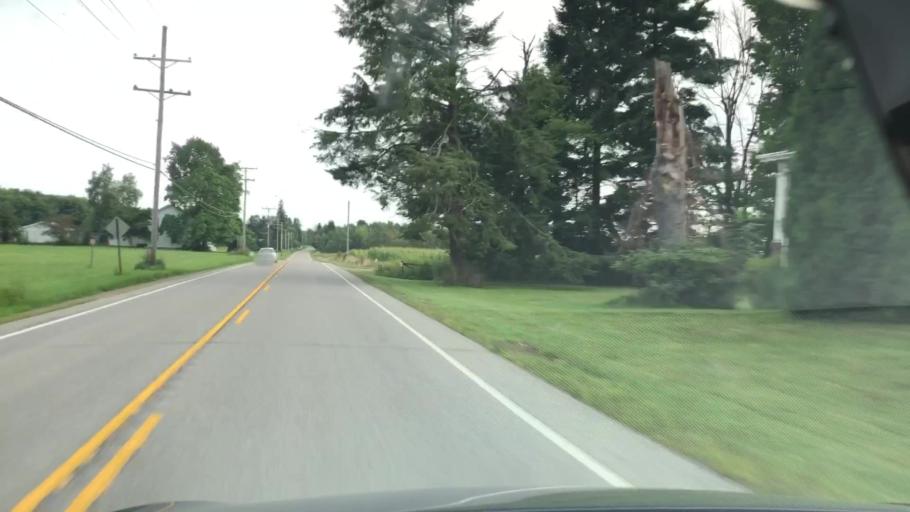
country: US
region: Pennsylvania
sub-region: Crawford County
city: Titusville
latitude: 41.5868
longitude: -79.6856
